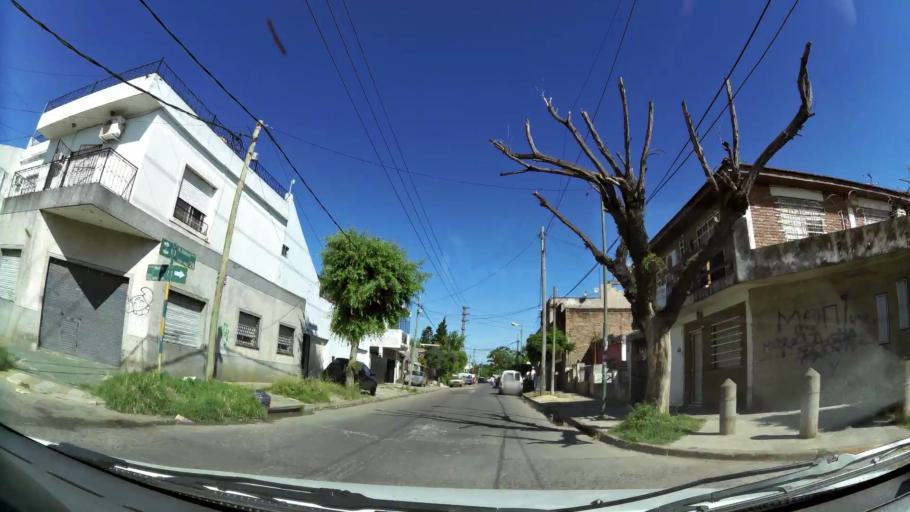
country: AR
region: Buenos Aires
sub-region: Partido de General San Martin
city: General San Martin
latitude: -34.5102
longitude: -58.5813
